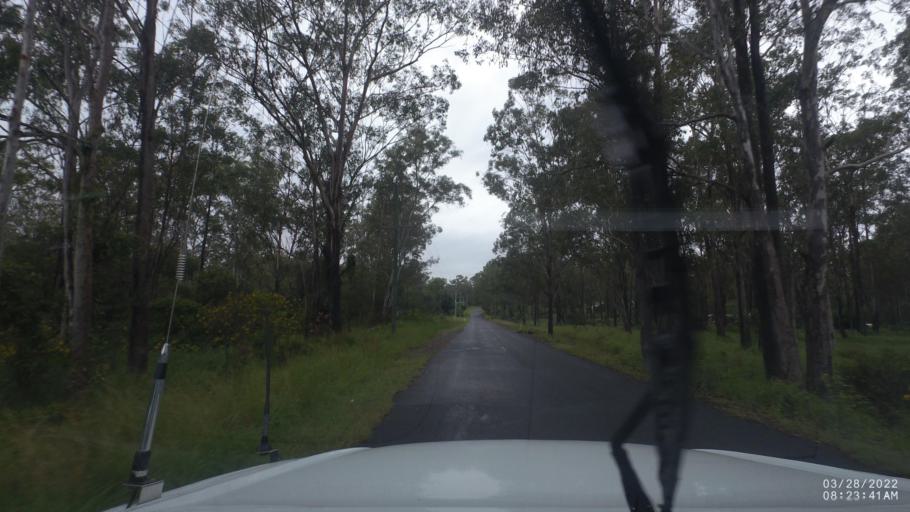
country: AU
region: Queensland
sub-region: Logan
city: Cedar Vale
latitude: -27.8406
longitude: 153.0506
